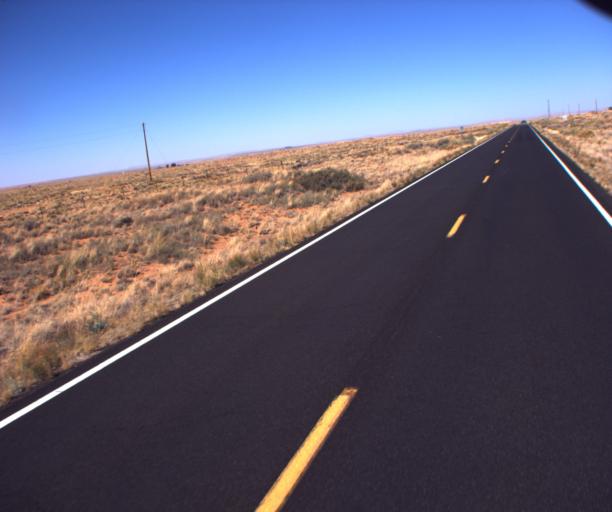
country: US
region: Arizona
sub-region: Navajo County
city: Dilkon
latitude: 35.4994
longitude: -110.4341
